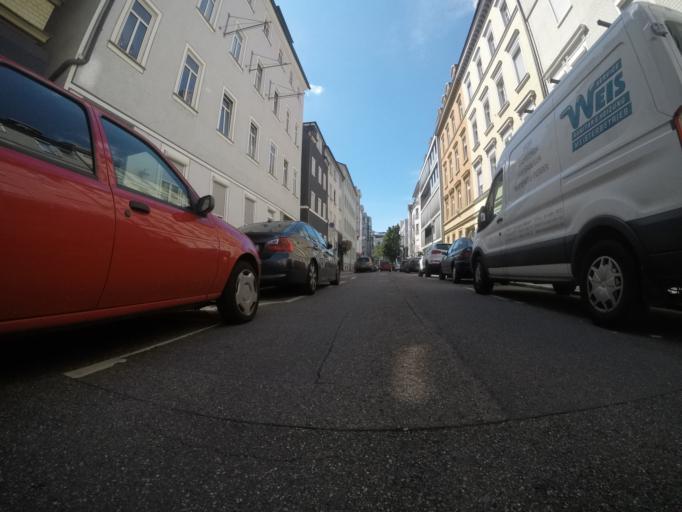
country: DE
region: Baden-Wuerttemberg
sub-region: Regierungsbezirk Stuttgart
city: Stuttgart
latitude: 48.7713
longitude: 9.1761
